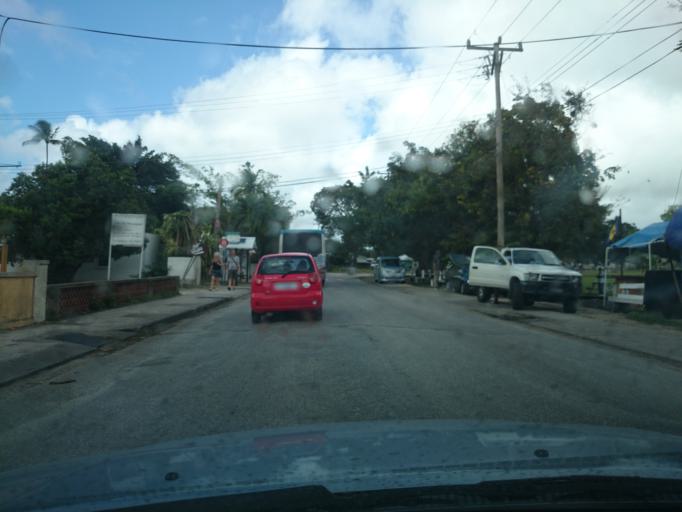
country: BB
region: Saint James
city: Holetown
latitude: 13.1886
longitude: -59.6368
